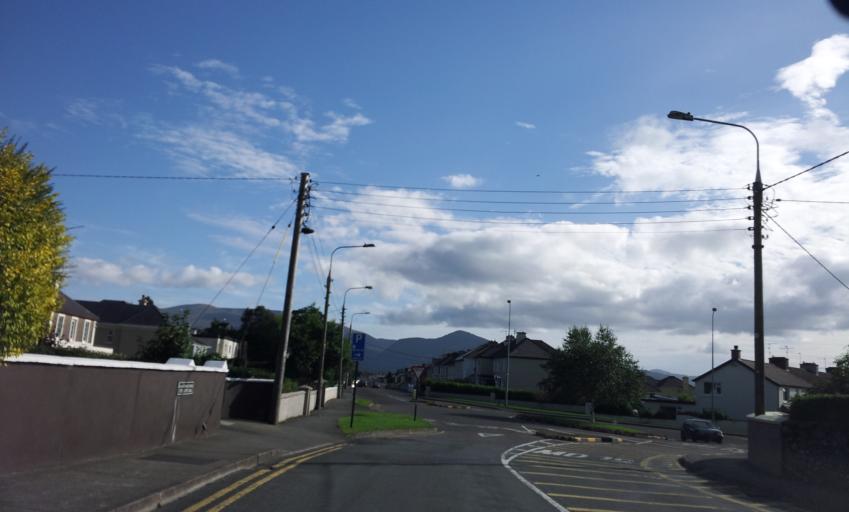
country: IE
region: Munster
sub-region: Ciarrai
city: Cill Airne
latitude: 52.0644
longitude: -9.5061
